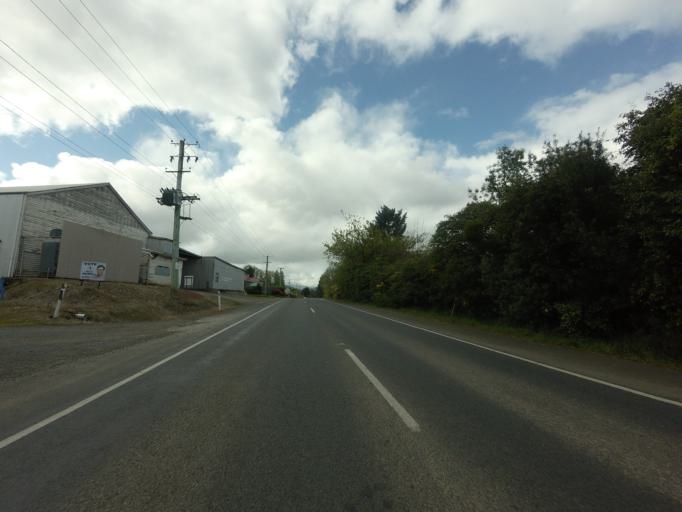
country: AU
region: Tasmania
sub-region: Huon Valley
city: Franklin
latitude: -43.0976
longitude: 147.0059
